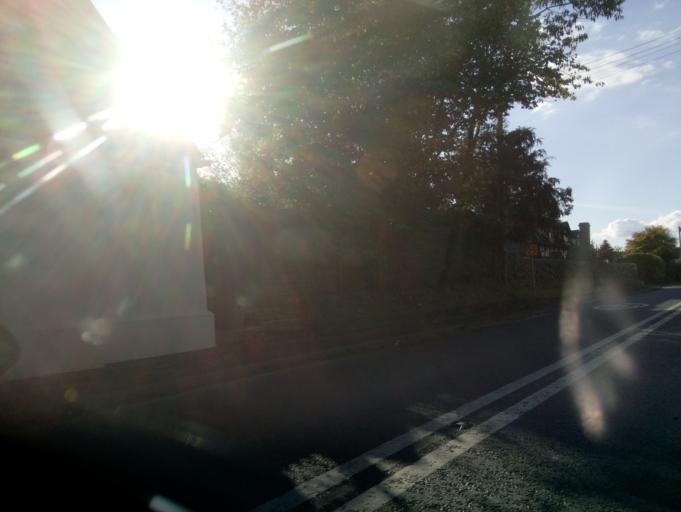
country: GB
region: England
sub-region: Herefordshire
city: Dorstone
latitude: 52.1172
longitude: -3.0263
